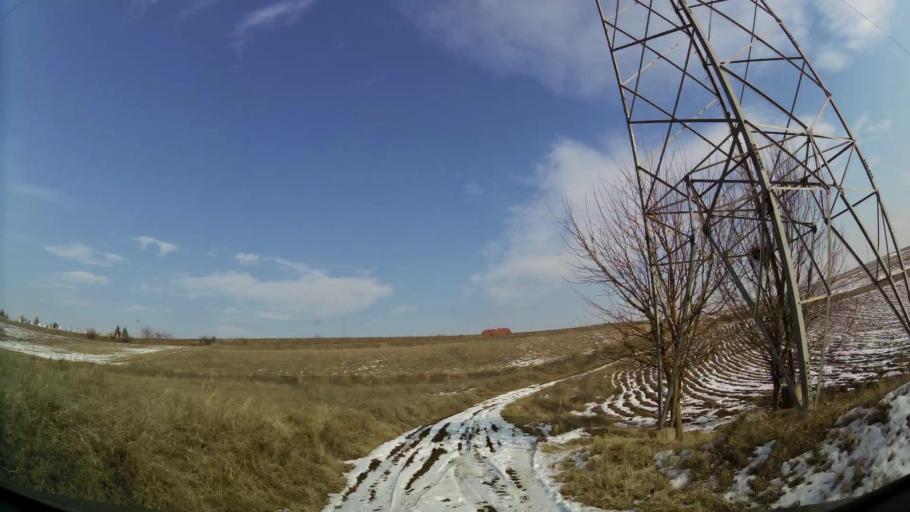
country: MK
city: Creshevo
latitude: 42.0172
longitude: 21.4953
